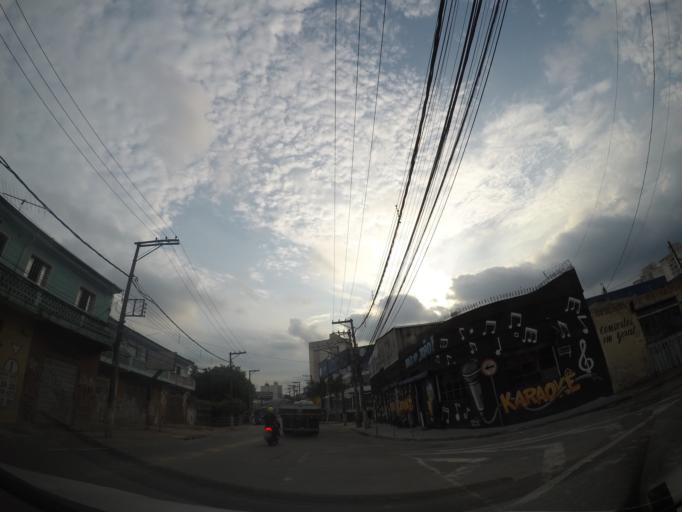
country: BR
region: Sao Paulo
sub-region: Guarulhos
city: Guarulhos
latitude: -23.4652
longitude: -46.5136
